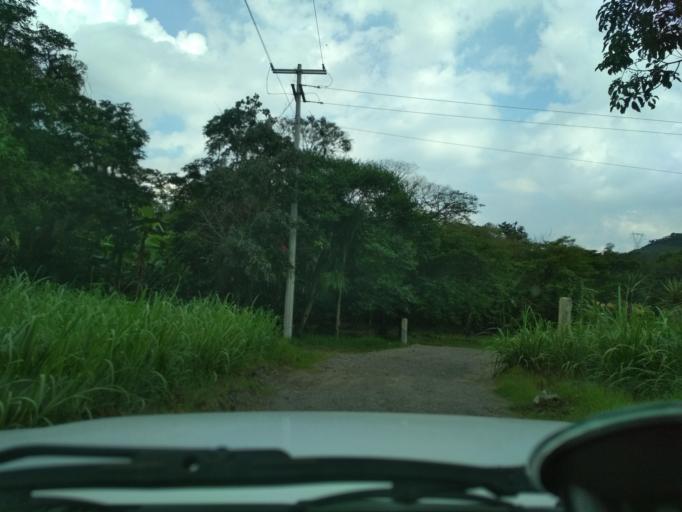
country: MX
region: Veracruz
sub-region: Ixtaczoquitlan
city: Buenavista
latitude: 18.9015
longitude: -97.0267
